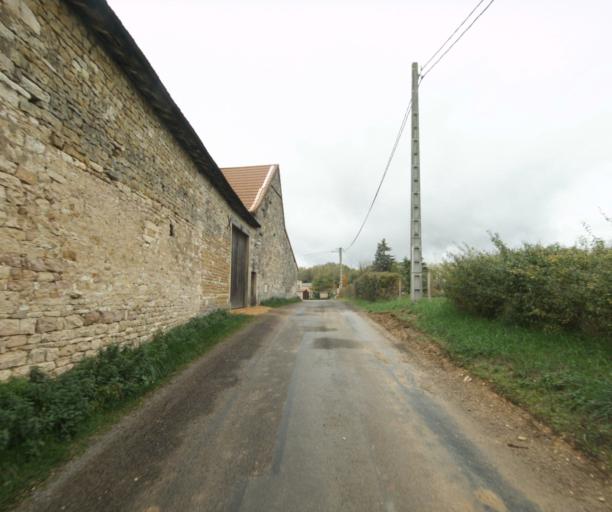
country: FR
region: Rhone-Alpes
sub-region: Departement de l'Ain
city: Pont-de-Vaux
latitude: 46.4714
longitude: 4.8881
